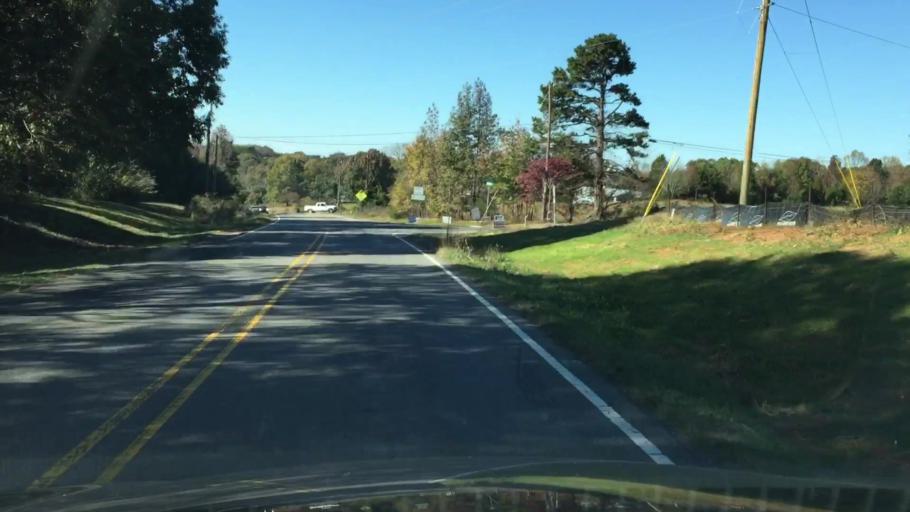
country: US
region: North Carolina
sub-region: Iredell County
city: Mooresville
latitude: 35.5519
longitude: -80.7755
